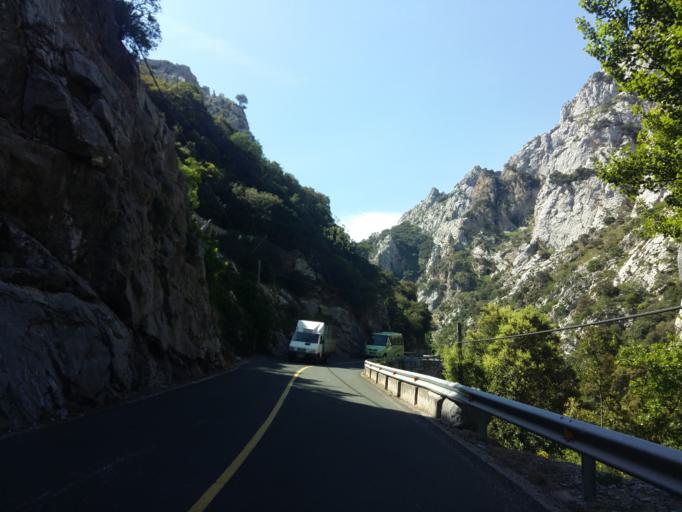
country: ES
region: Cantabria
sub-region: Provincia de Cantabria
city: Potes
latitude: 43.2089
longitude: -4.5944
